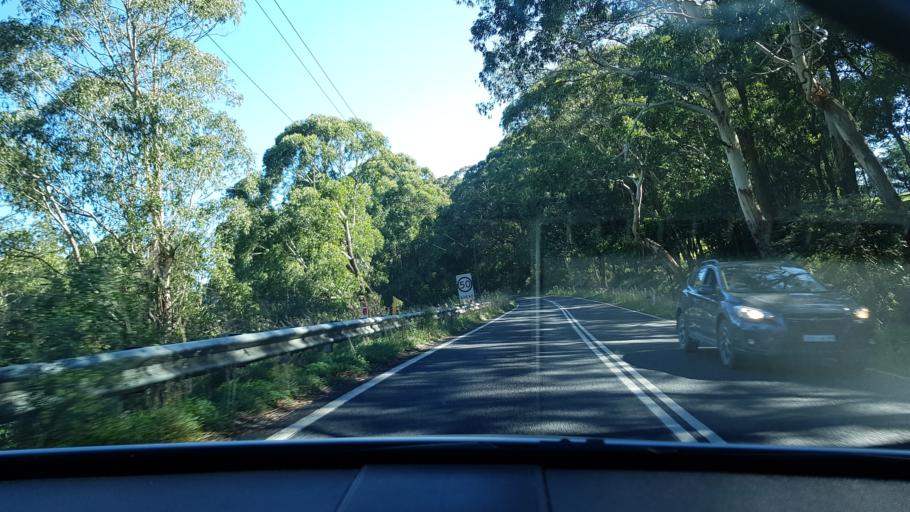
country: AU
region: New South Wales
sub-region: Lithgow
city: Bowenfels
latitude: -33.6406
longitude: 150.0524
